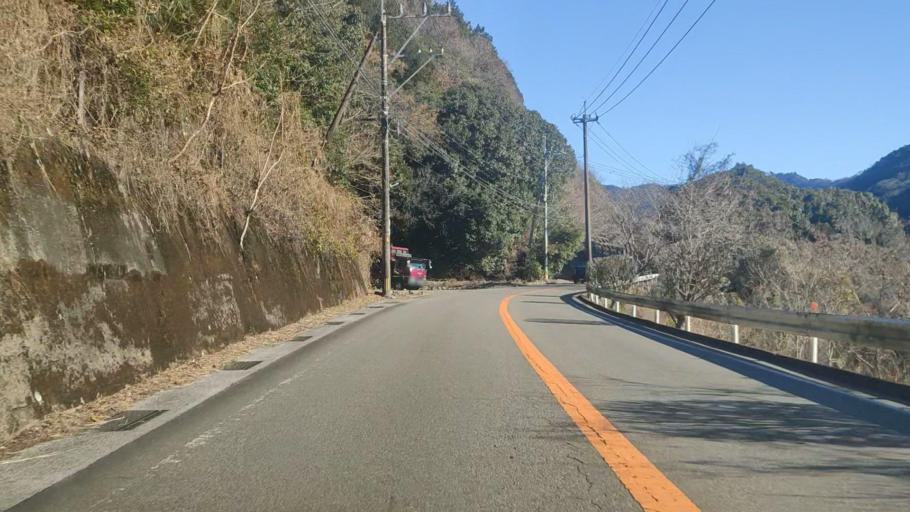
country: JP
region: Miyazaki
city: Nobeoka
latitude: 32.6194
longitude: 131.7042
